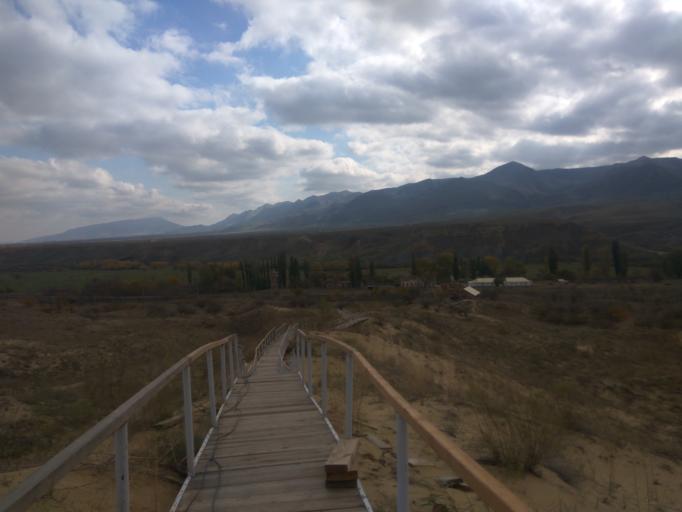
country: RU
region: Dagestan
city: Korkmaskala
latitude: 43.0059
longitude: 47.2348
